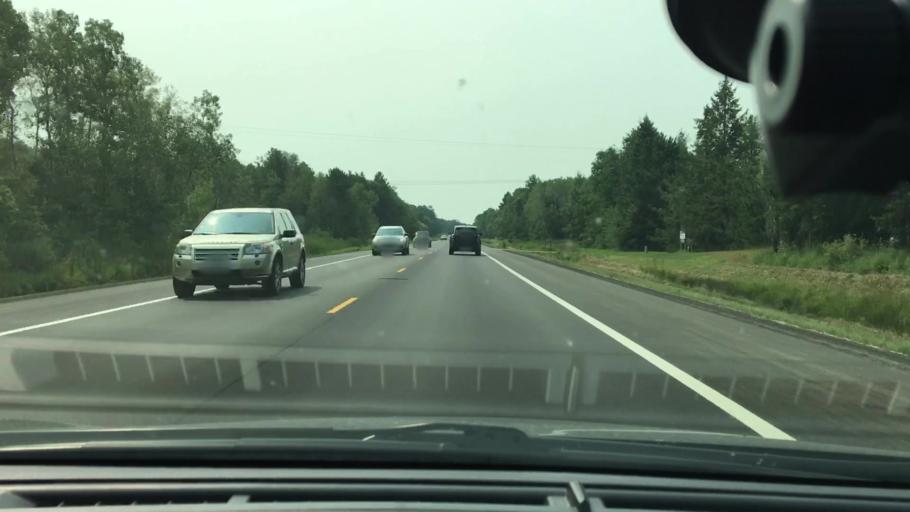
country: US
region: Minnesota
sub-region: Crow Wing County
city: Brainerd
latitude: 46.4463
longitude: -94.1719
